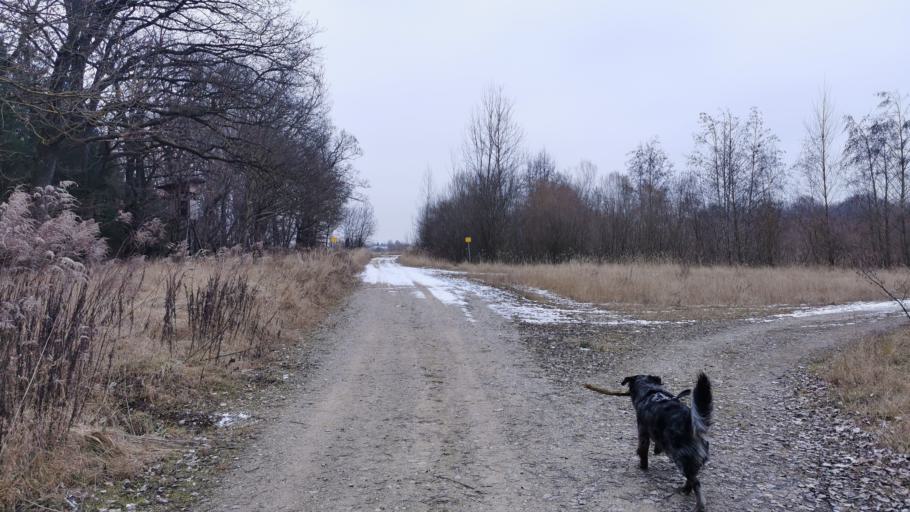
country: DE
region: Bavaria
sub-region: Upper Bavaria
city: Kirchheim bei Muenchen
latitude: 48.1933
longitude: 11.7624
